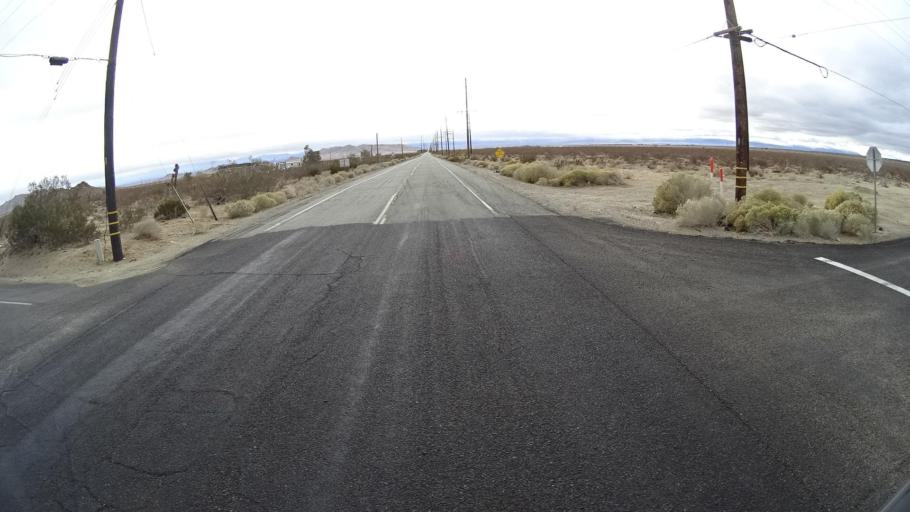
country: US
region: California
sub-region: Kern County
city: Rosamond
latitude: 34.9509
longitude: -118.2915
